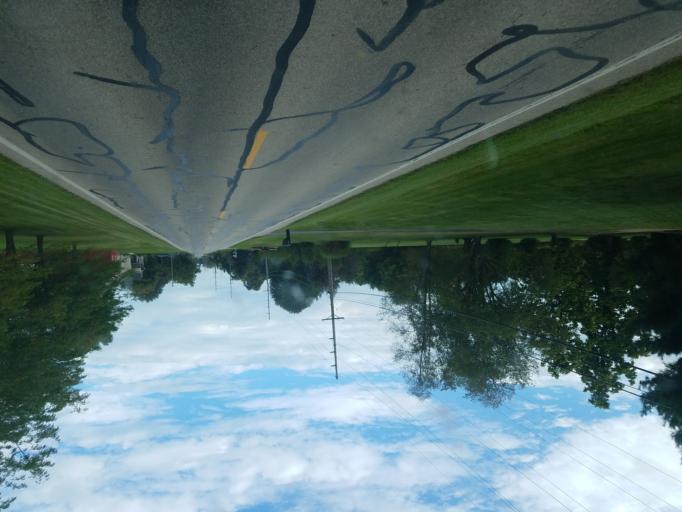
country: US
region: Ohio
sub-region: Delaware County
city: Sunbury
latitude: 40.2524
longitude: -82.7886
